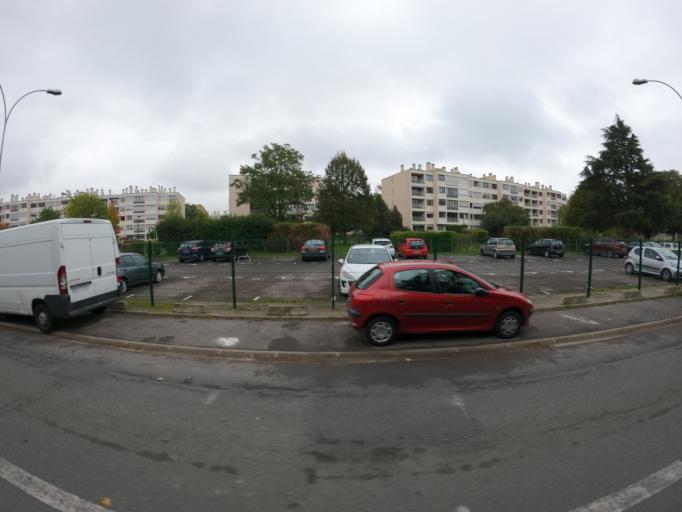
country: FR
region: Ile-de-France
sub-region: Departement du Val-de-Marne
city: Chennevieres-sur-Marne
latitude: 48.7870
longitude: 2.5259
